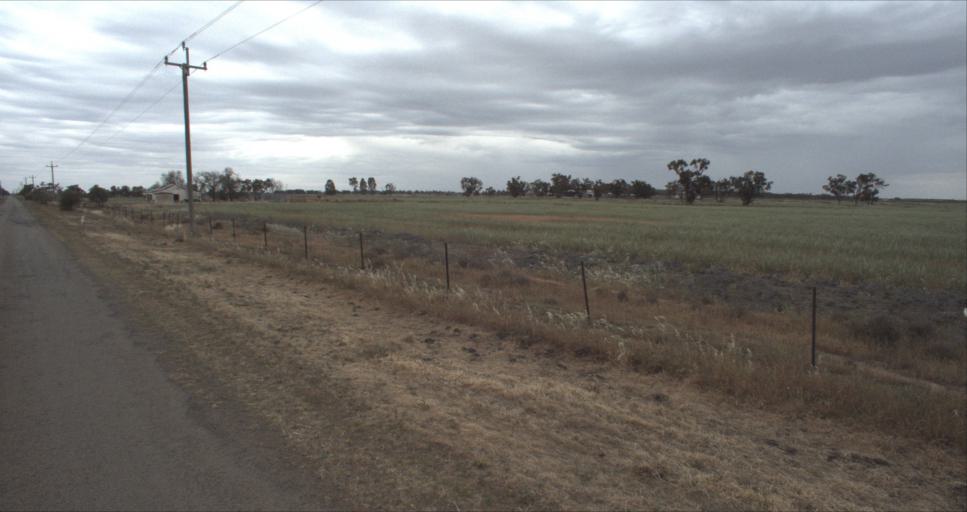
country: AU
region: New South Wales
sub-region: Leeton
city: Leeton
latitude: -34.4110
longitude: 146.3403
